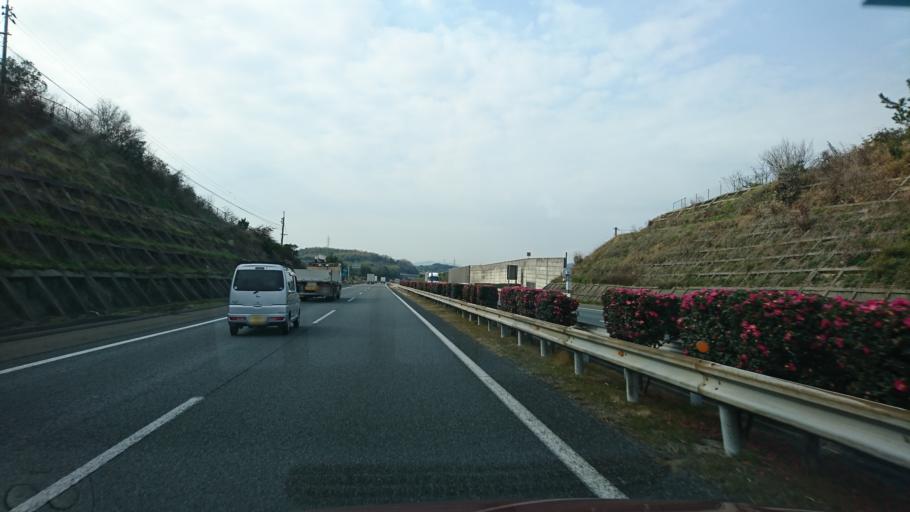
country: JP
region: Hiroshima
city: Kannabecho-yahiro
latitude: 34.5339
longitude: 133.4547
